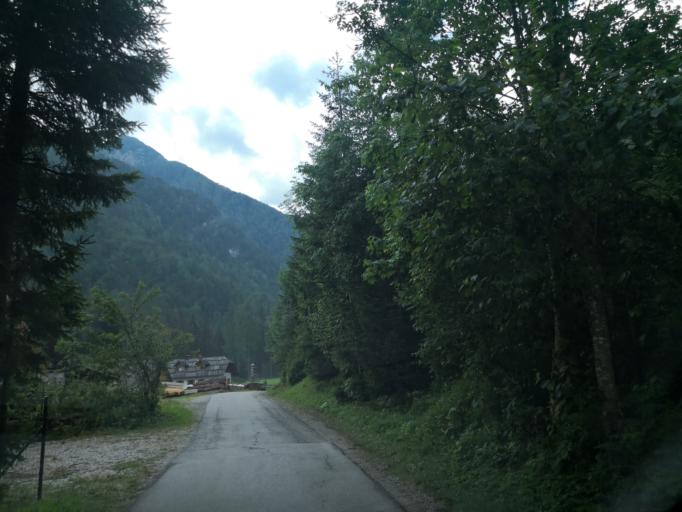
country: SI
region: Jezersko
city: Zgornje Jezersko
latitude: 46.4004
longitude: 14.5227
